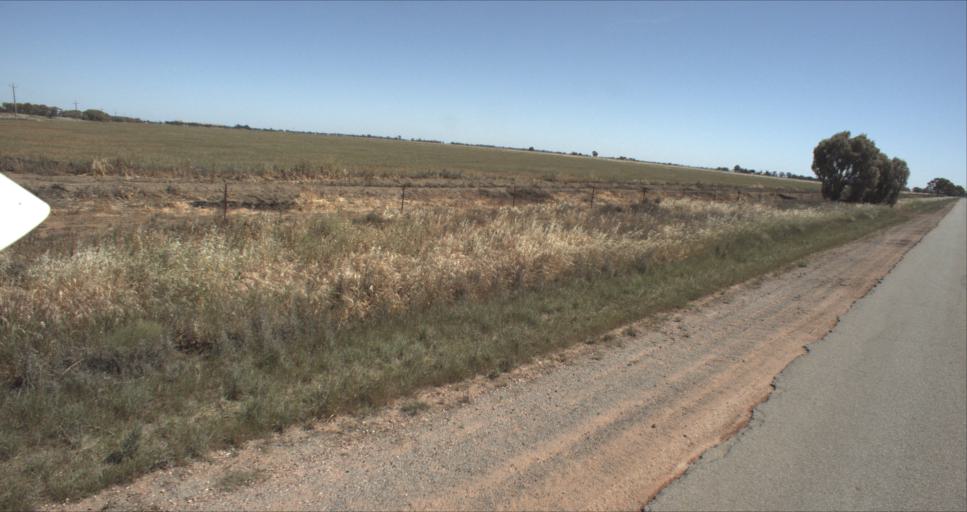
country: AU
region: New South Wales
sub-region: Leeton
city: Leeton
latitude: -34.5667
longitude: 146.3117
